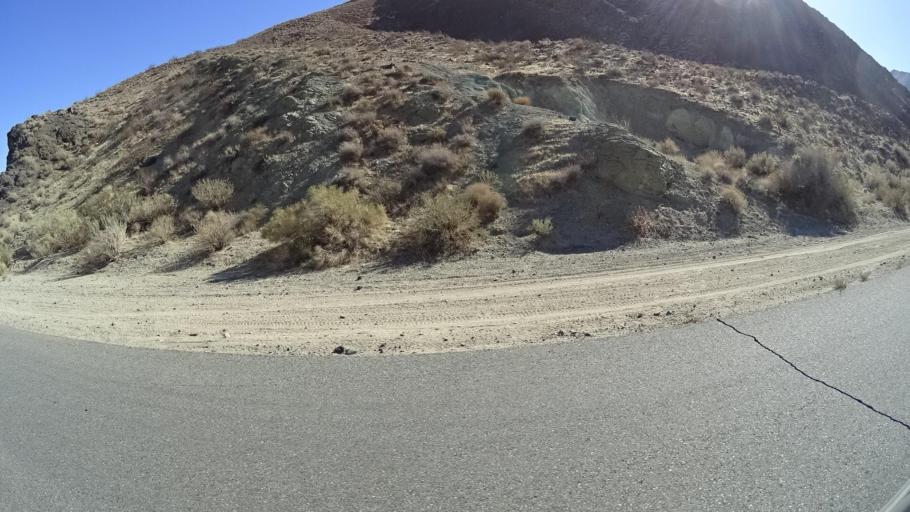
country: US
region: California
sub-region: Kern County
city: California City
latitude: 35.3174
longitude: -118.0842
